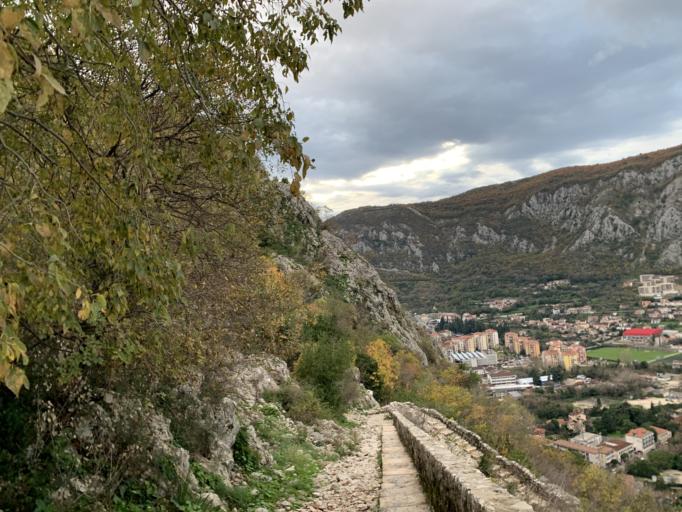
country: ME
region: Kotor
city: Kotor
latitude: 42.4239
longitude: 18.7742
